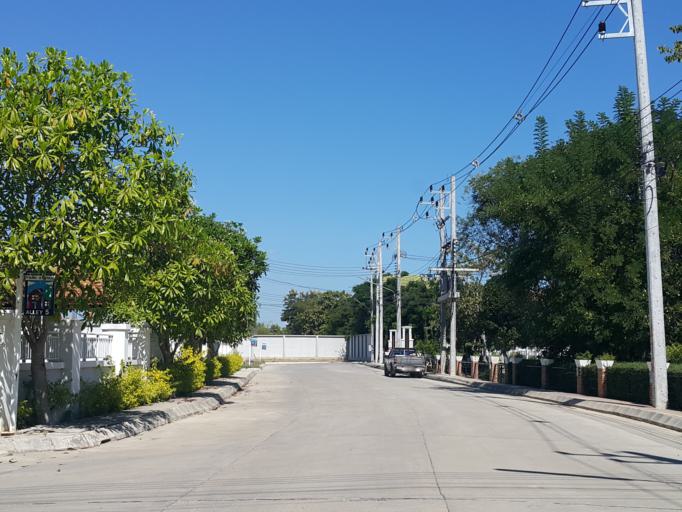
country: TH
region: Chiang Mai
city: San Sai
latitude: 18.8112
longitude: 99.0632
